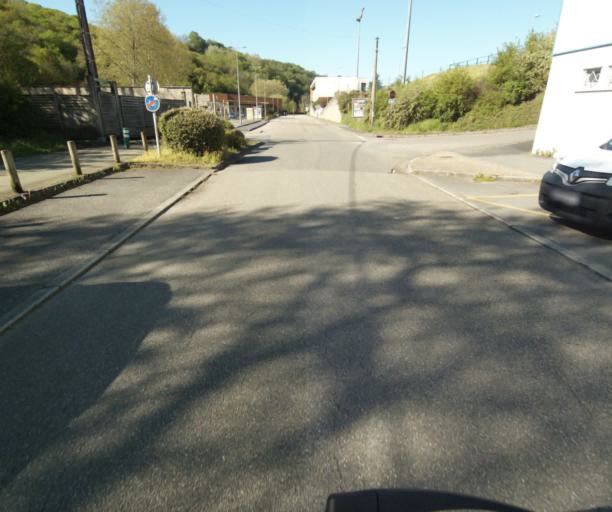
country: FR
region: Limousin
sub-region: Departement de la Correze
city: Tulle
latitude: 45.2787
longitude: 1.7844
